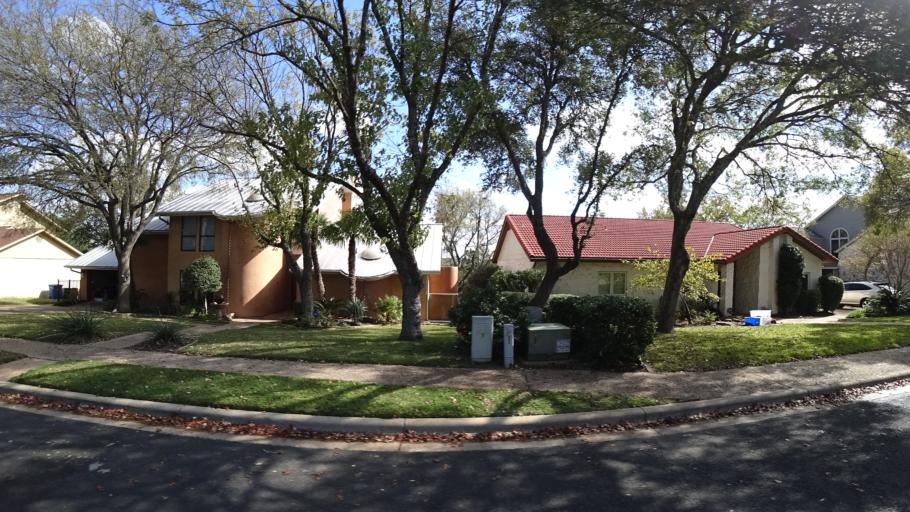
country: US
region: Texas
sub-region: Williamson County
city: Jollyville
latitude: 30.4238
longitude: -97.8003
